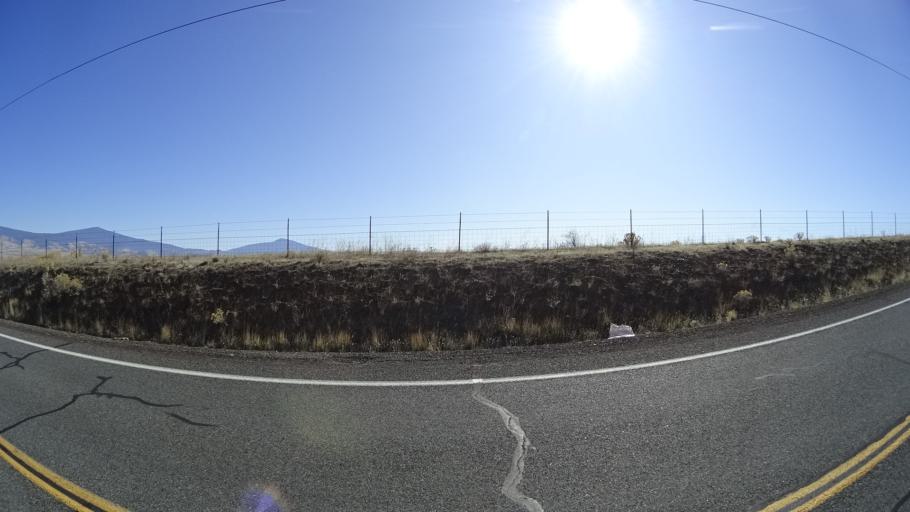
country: US
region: California
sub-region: Siskiyou County
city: Montague
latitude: 41.8062
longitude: -122.4999
